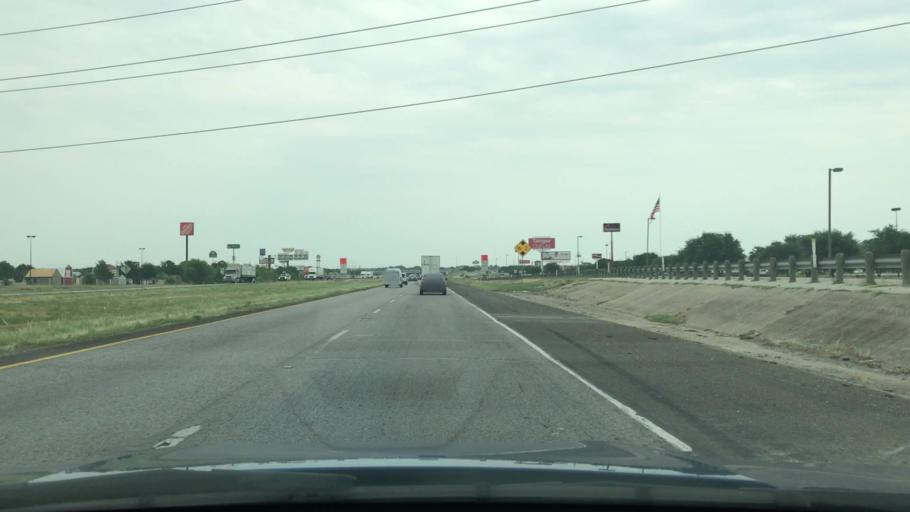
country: US
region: Texas
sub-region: Kaufman County
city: Terrell
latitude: 32.7050
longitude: -96.2845
